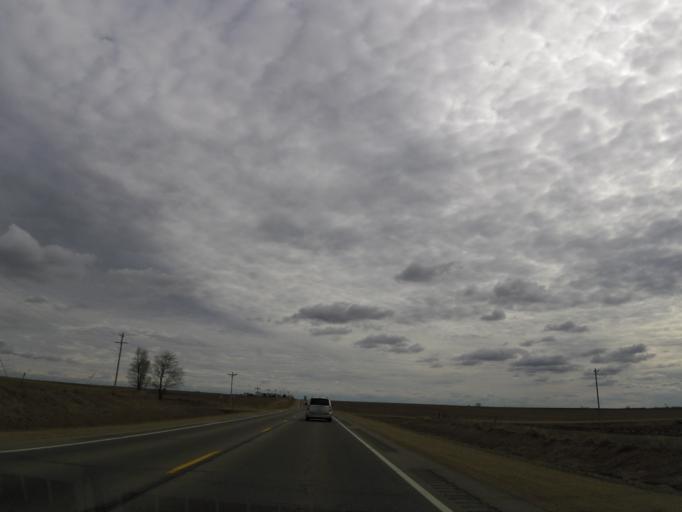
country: US
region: Iowa
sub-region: Chickasaw County
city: New Hampton
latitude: 43.1429
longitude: -92.2990
